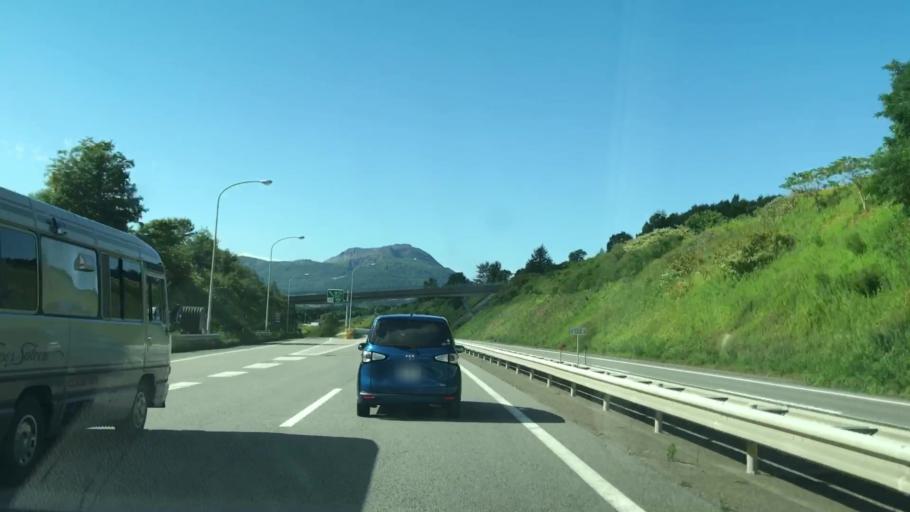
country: JP
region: Hokkaido
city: Date
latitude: 42.4796
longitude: 140.8994
